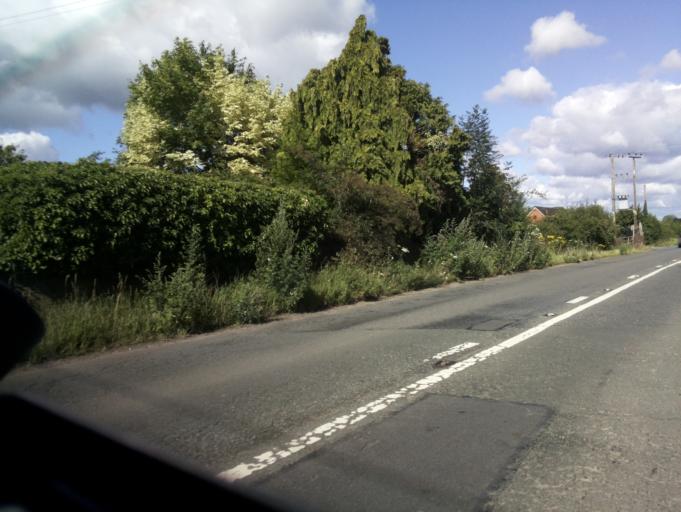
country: GB
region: England
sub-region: Gloucestershire
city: Newent
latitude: 51.9079
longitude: -2.3372
